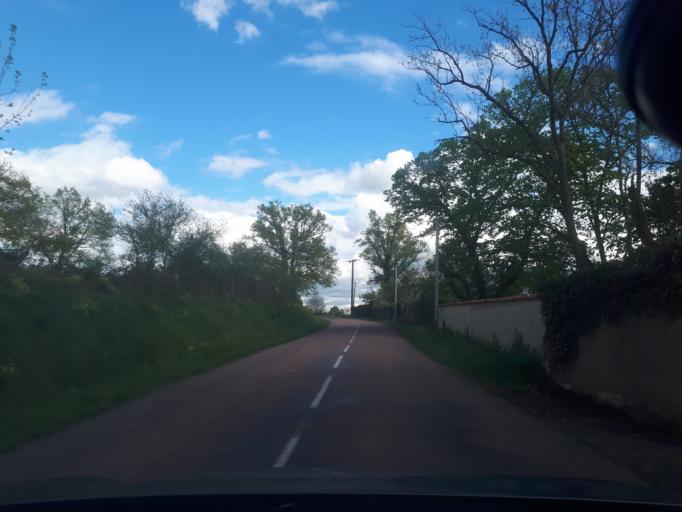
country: FR
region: Rhone-Alpes
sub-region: Departement de la Loire
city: Pouilly-les-Feurs
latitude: 45.8112
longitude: 4.2166
